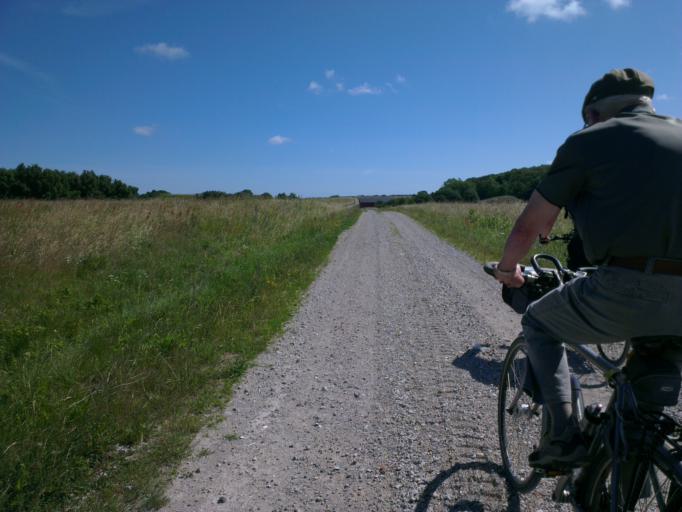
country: DK
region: Capital Region
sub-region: Frederikssund Kommune
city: Jaegerspris
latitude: 55.8767
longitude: 11.9425
